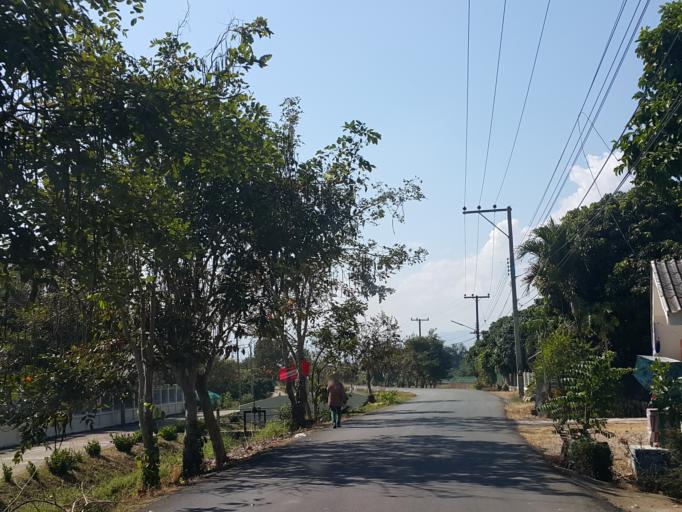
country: TH
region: Chiang Mai
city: Mae Taeng
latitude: 19.0389
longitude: 98.9761
